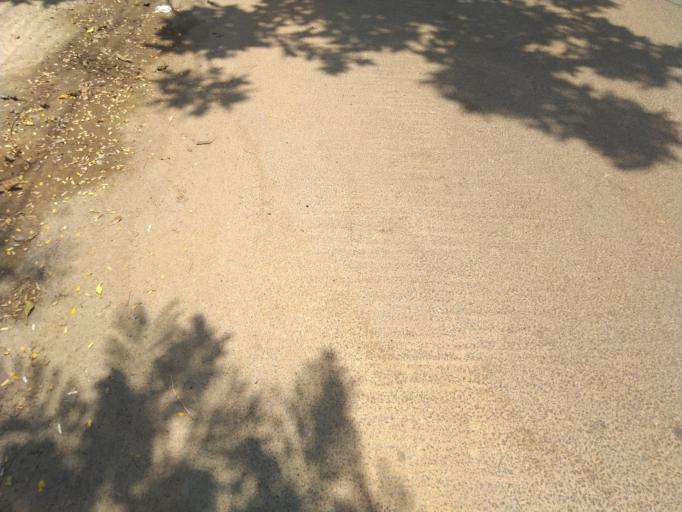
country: IN
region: Telangana
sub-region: Rangareddi
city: Kukatpalli
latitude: 17.4393
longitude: 78.4057
